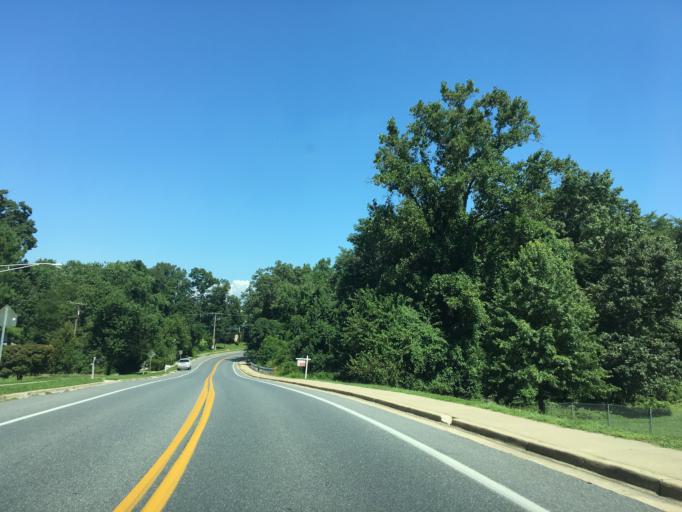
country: US
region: Maryland
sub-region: Anne Arundel County
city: Arden on the Severn
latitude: 39.0835
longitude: -76.5714
